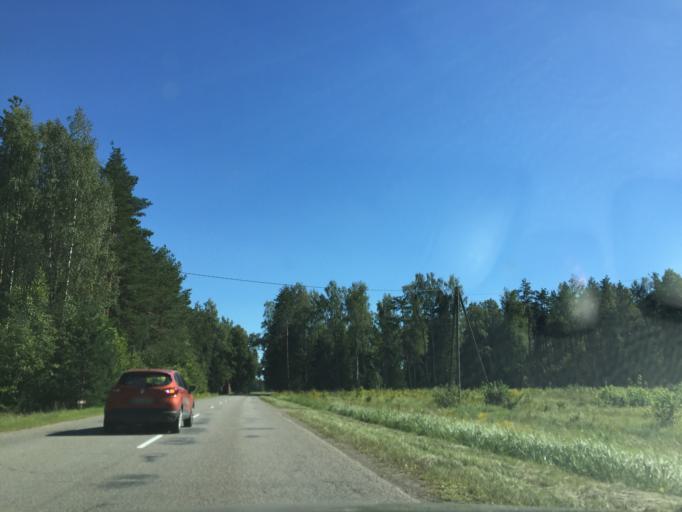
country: LV
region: Akniste
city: Akniste
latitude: 56.1364
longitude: 25.8201
